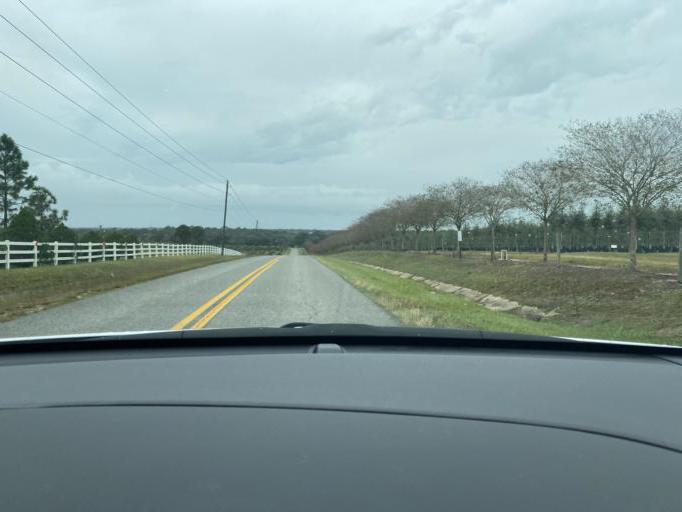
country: US
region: Florida
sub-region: Lake County
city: Groveland
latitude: 28.5874
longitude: -81.8459
